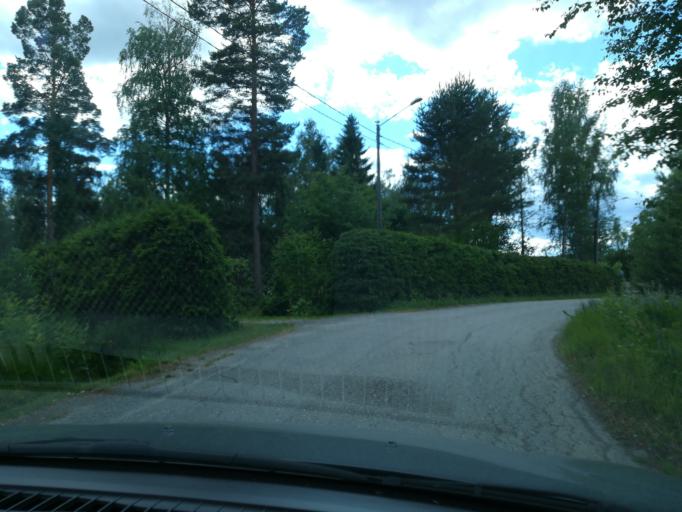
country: FI
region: Southern Savonia
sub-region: Mikkeli
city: Hirvensalmi
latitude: 61.6476
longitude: 26.7732
